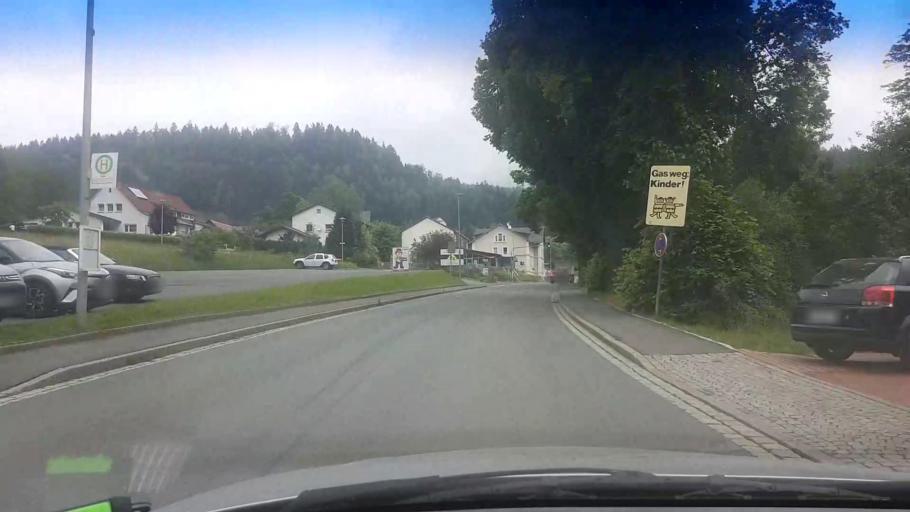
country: DE
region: Bavaria
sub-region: Upper Franconia
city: Warmensteinach
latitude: 49.9977
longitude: 11.7793
